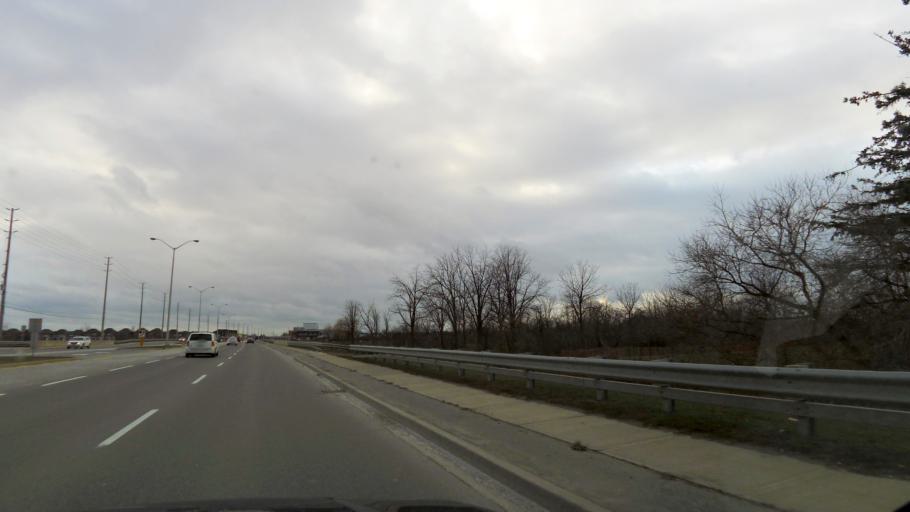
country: CA
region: Ontario
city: Brampton
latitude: 43.7875
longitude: -79.6952
